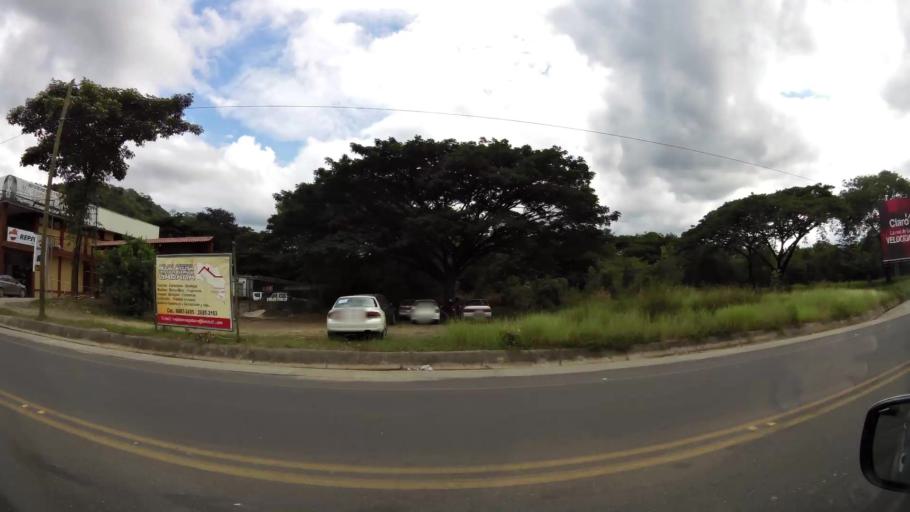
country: CR
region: Guanacaste
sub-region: Canton de Nicoya
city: Nicoya
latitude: 10.1569
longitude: -85.4491
